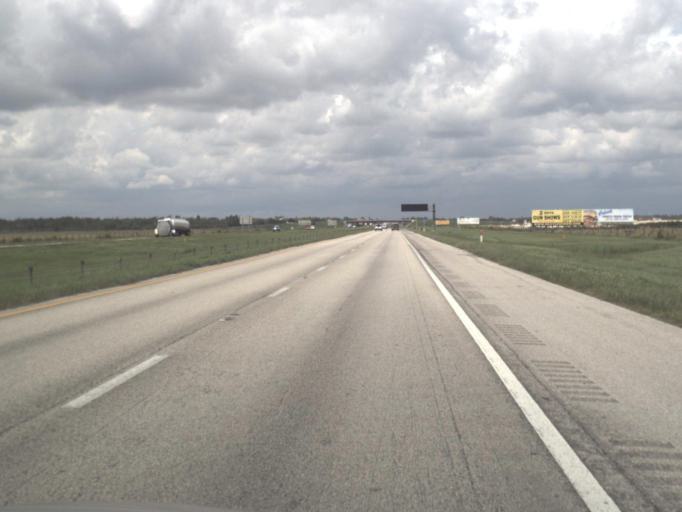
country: US
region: Florida
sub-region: Charlotte County
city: Punta Gorda
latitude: 26.9075
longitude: -82.0093
